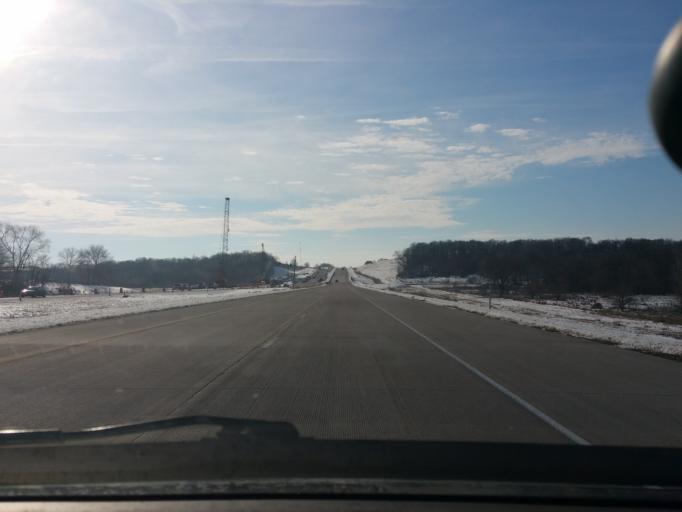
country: US
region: Iowa
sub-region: Warren County
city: Norwalk
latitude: 41.4606
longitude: -93.7803
